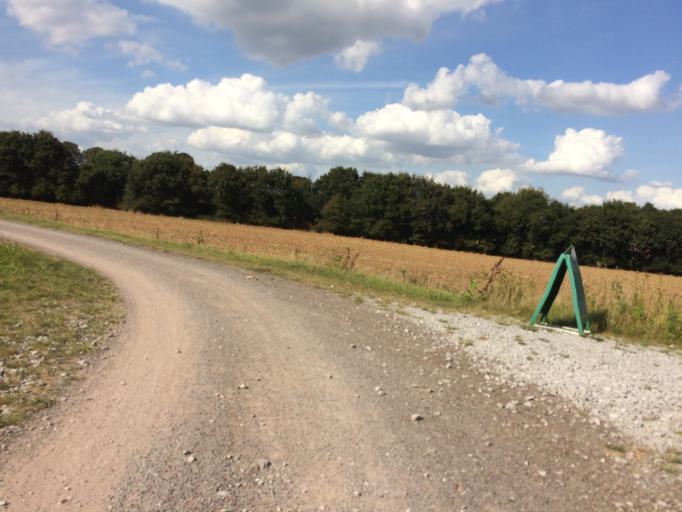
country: DE
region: North Rhine-Westphalia
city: Marl
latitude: 51.7018
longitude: 7.0800
